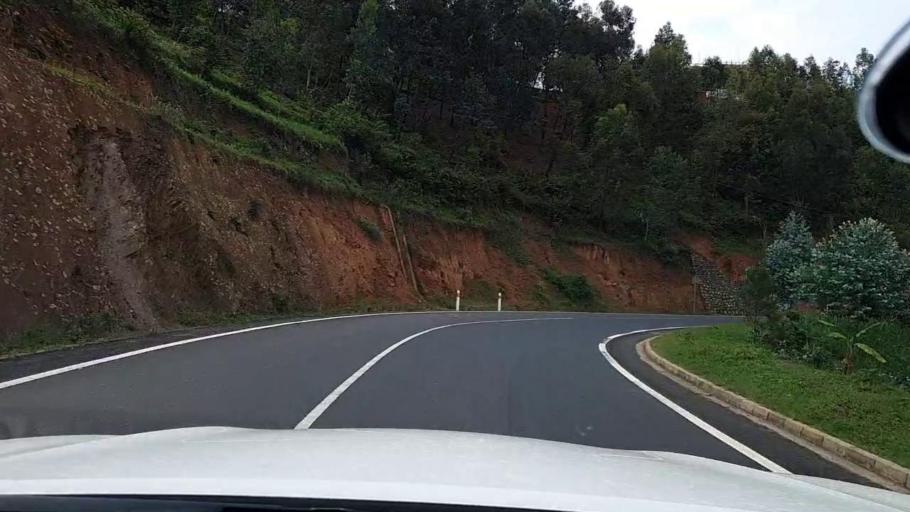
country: RW
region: Western Province
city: Kibuye
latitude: -2.1753
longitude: 29.2915
